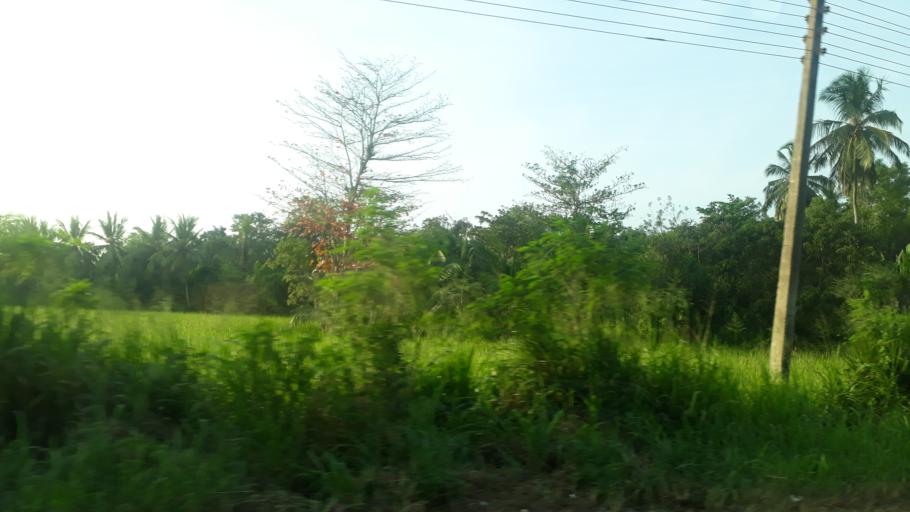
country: LK
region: North Central
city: Anuradhapura
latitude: 8.2949
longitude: 80.3743
